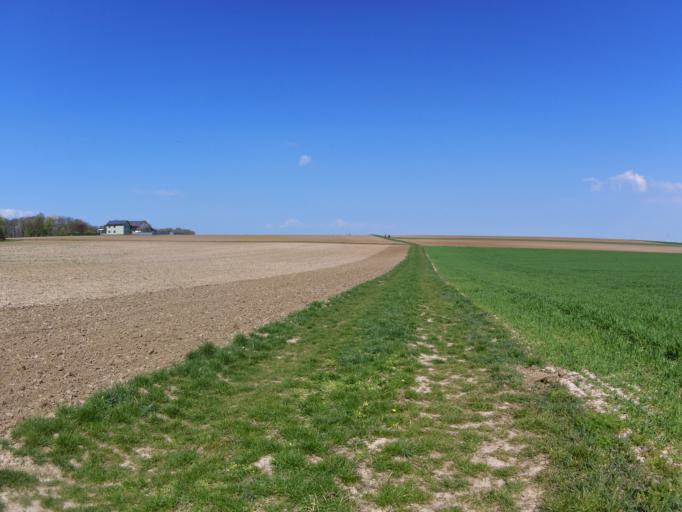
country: DE
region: Bavaria
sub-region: Regierungsbezirk Unterfranken
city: Oberpleichfeld
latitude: 49.8418
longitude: 10.0760
